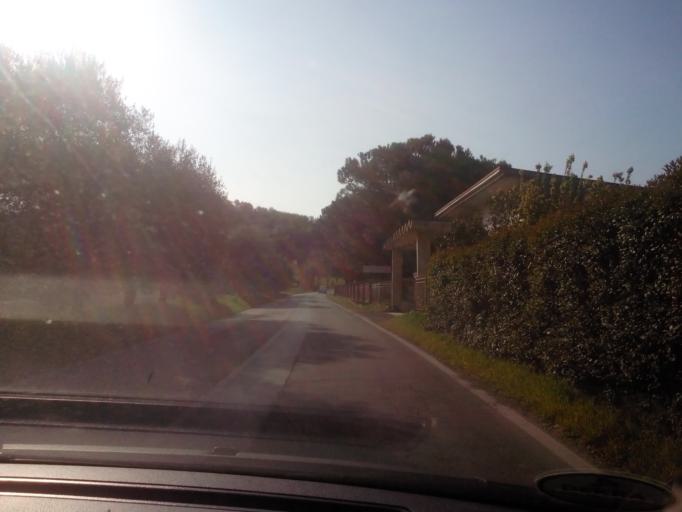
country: IT
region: Lombardy
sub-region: Provincia di Brescia
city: Padenghe sul Garda
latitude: 45.4877
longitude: 10.5160
